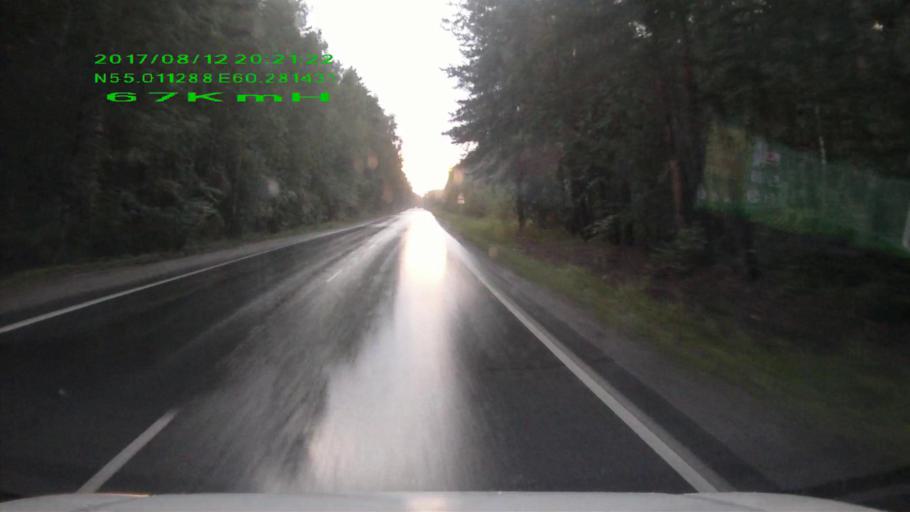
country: RU
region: Chelyabinsk
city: Chebarkul'
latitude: 55.0113
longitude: 60.2813
